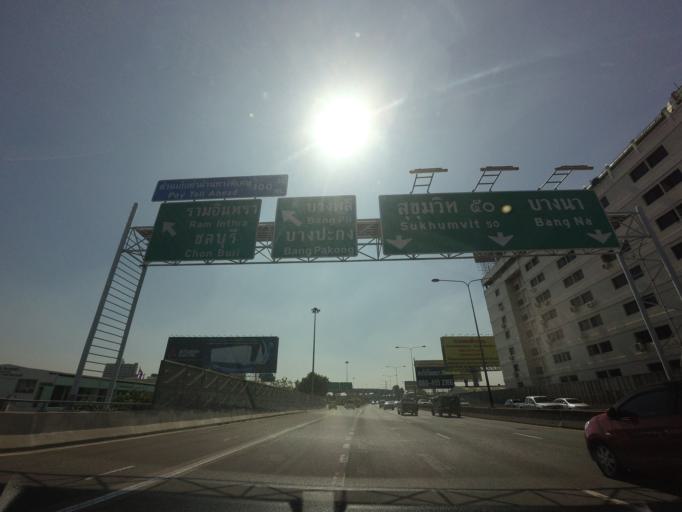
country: TH
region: Bangkok
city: Phra Khanong
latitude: 13.7045
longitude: 100.5893
